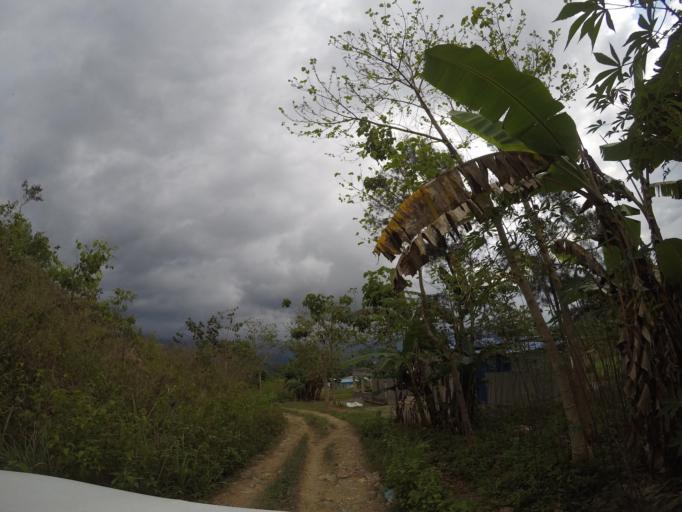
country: TL
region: Ermera
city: Gleno
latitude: -8.7077
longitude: 125.4519
